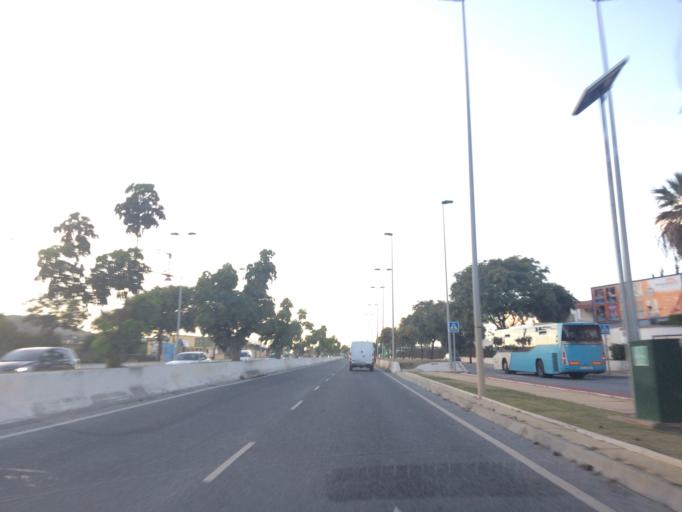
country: ES
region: Andalusia
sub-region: Provincia de Malaga
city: Torremolinos
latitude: 36.6583
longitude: -4.4893
